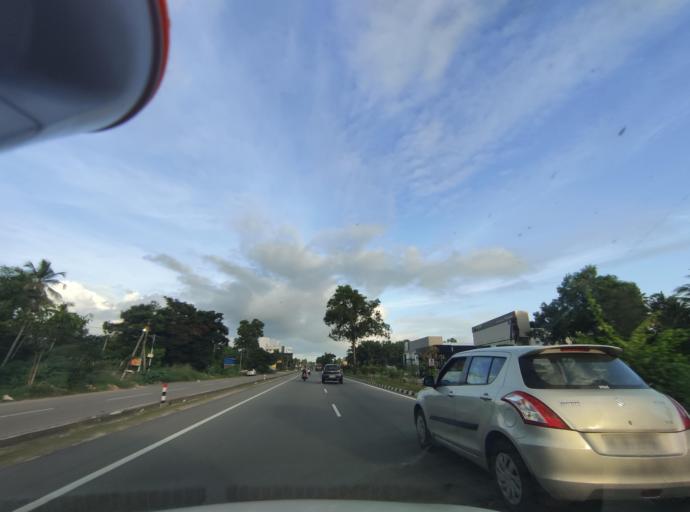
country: IN
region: Kerala
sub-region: Thiruvananthapuram
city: Thiruvananthapuram
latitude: 8.5036
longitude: 76.9110
